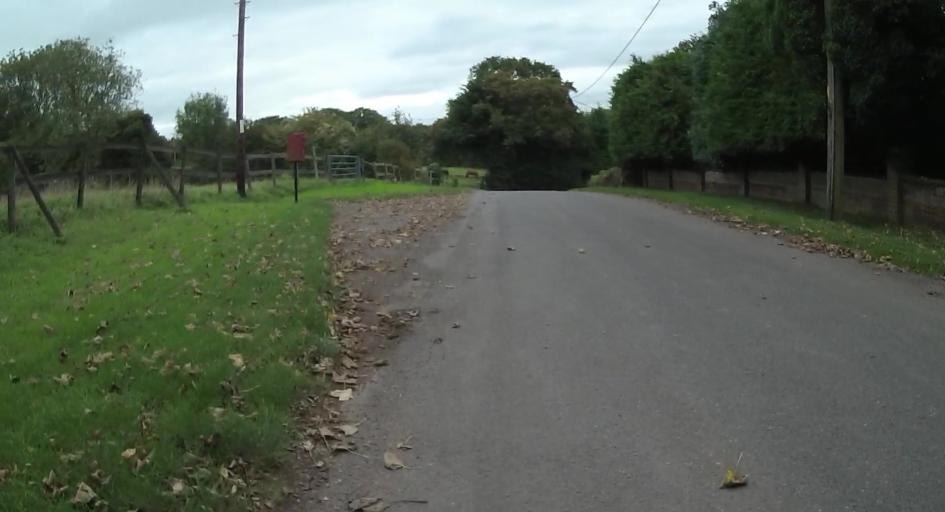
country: GB
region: England
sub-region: Hampshire
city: Four Marks
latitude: 51.1163
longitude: -1.0785
